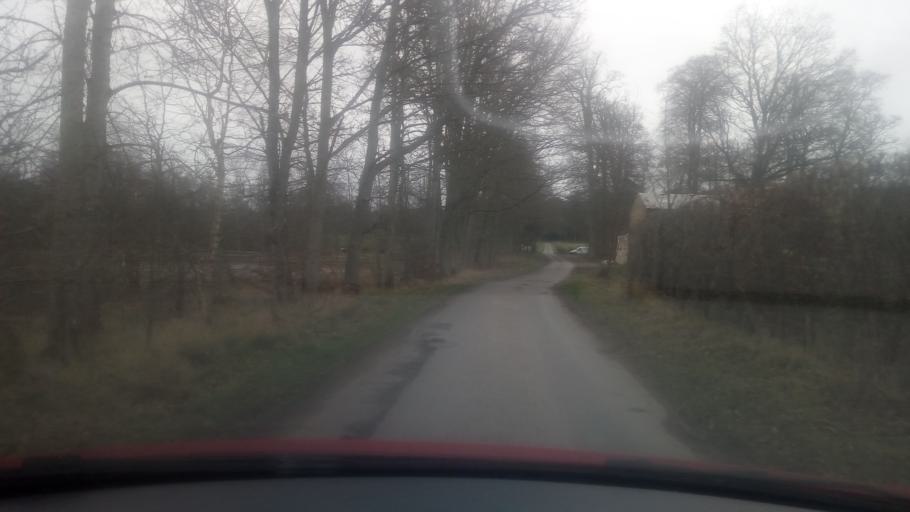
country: GB
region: Scotland
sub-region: The Scottish Borders
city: Jedburgh
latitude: 55.4497
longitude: -2.6396
